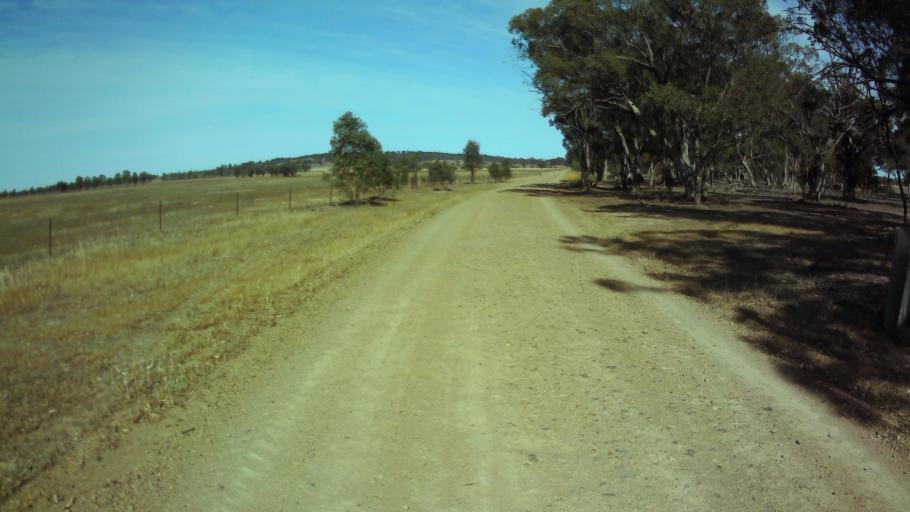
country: AU
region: New South Wales
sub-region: Weddin
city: Grenfell
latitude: -33.7833
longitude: 148.0757
